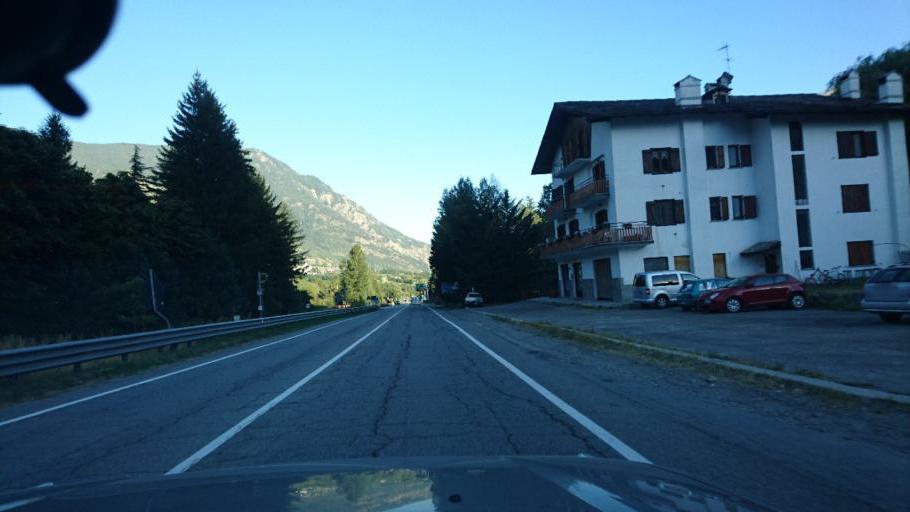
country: IT
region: Aosta Valley
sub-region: Valle d'Aosta
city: Morgex
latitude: 45.7523
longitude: 7.0470
